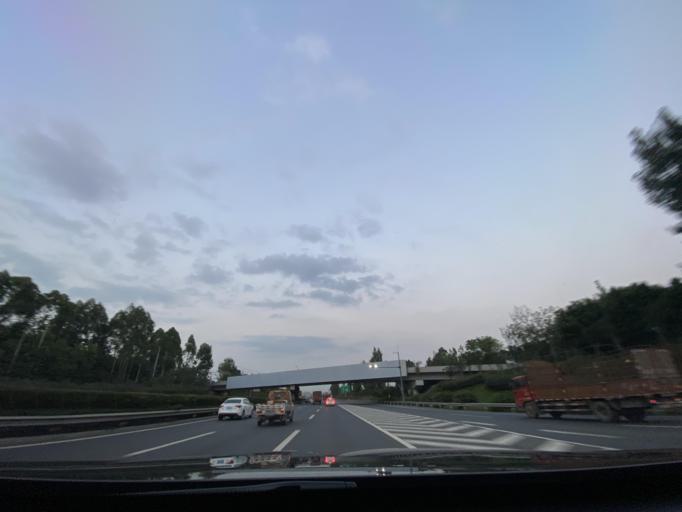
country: CN
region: Sichuan
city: Chengdu
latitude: 30.5703
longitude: 104.1129
